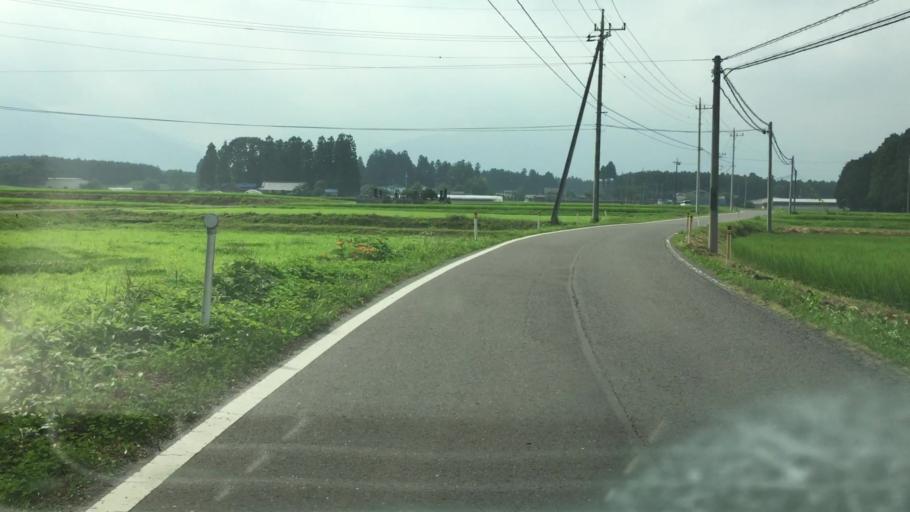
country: JP
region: Tochigi
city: Kuroiso
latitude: 36.9585
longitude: 139.9545
